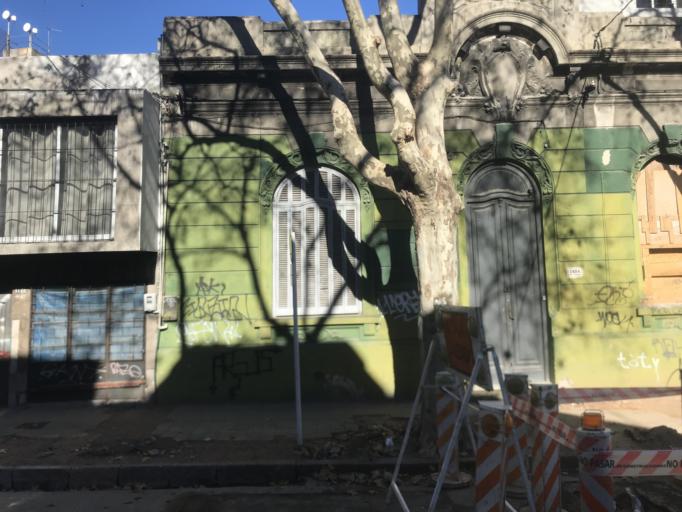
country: UY
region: Montevideo
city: Montevideo
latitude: -34.9025
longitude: -56.1852
